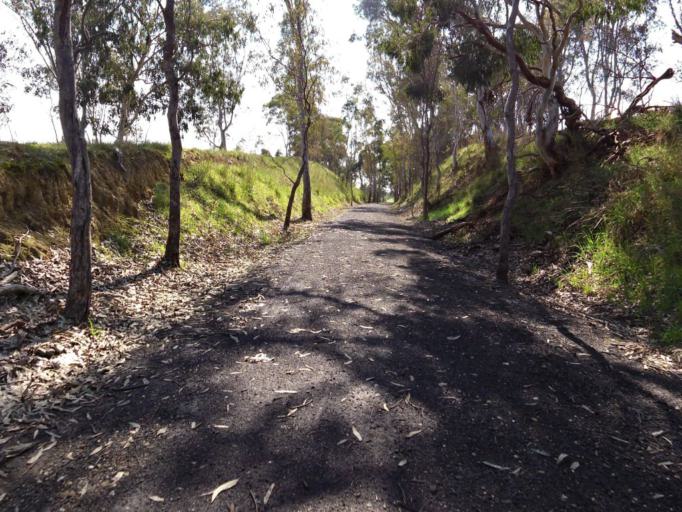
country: AU
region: Victoria
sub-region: Murrindindi
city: Alexandra
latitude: -37.1321
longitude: 145.5935
